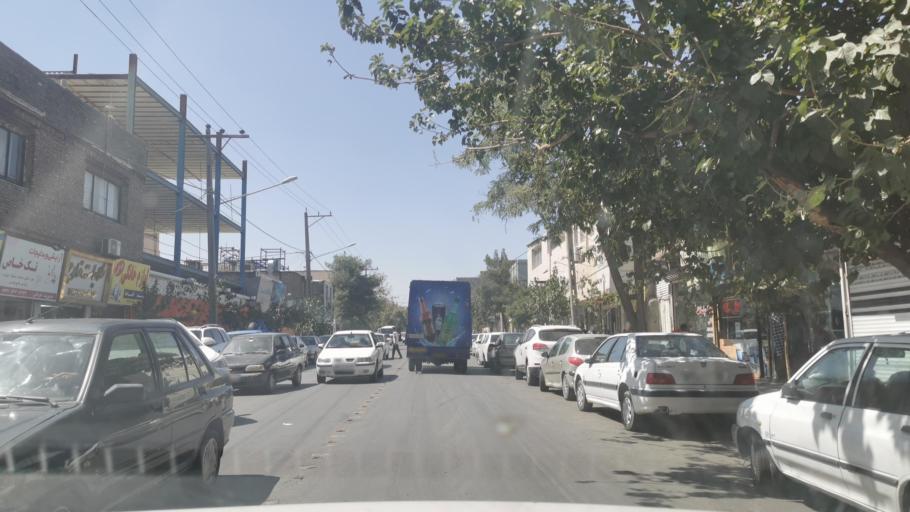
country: IR
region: Razavi Khorasan
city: Mashhad
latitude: 36.3591
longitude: 59.5499
